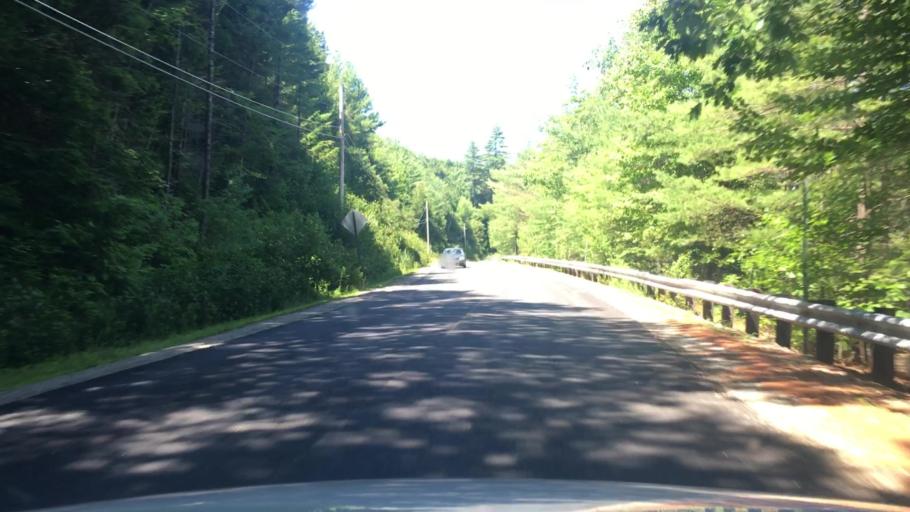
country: US
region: New Hampshire
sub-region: Merrimack County
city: Hopkinton
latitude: 43.2386
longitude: -71.6286
